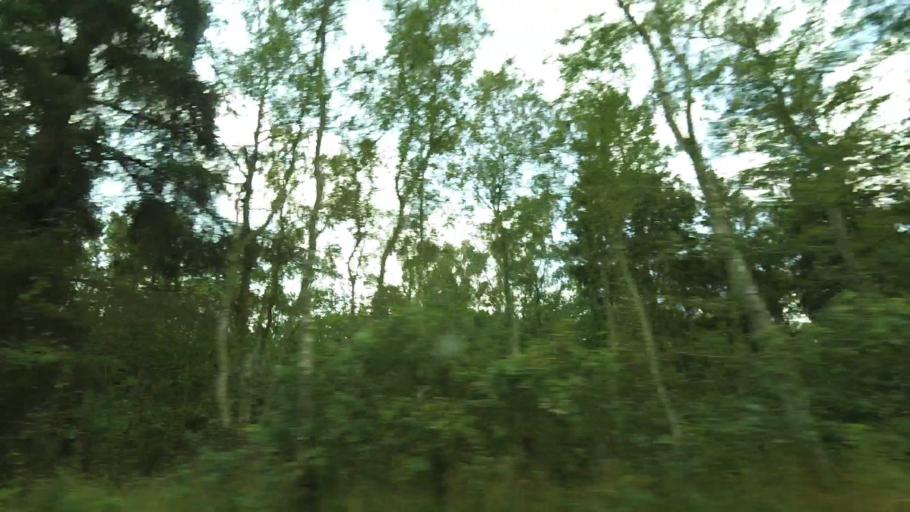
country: DK
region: Central Jutland
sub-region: Norddjurs Kommune
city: Auning
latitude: 56.5112
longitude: 10.4123
